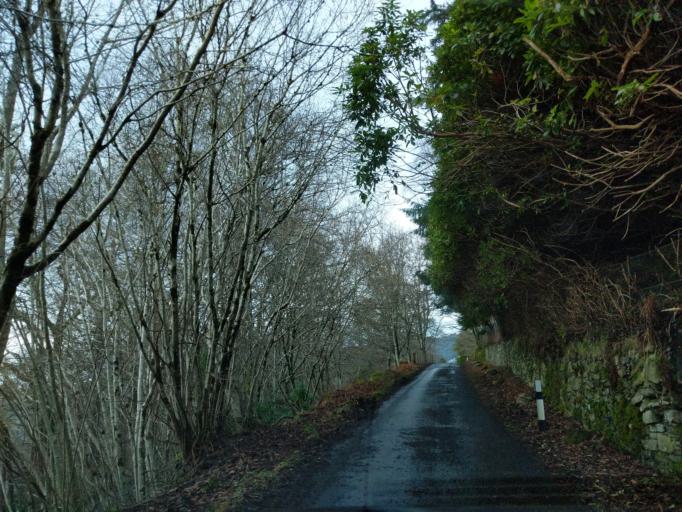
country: GB
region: Scotland
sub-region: Perth and Kinross
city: Comrie
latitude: 56.5742
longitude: -4.0688
